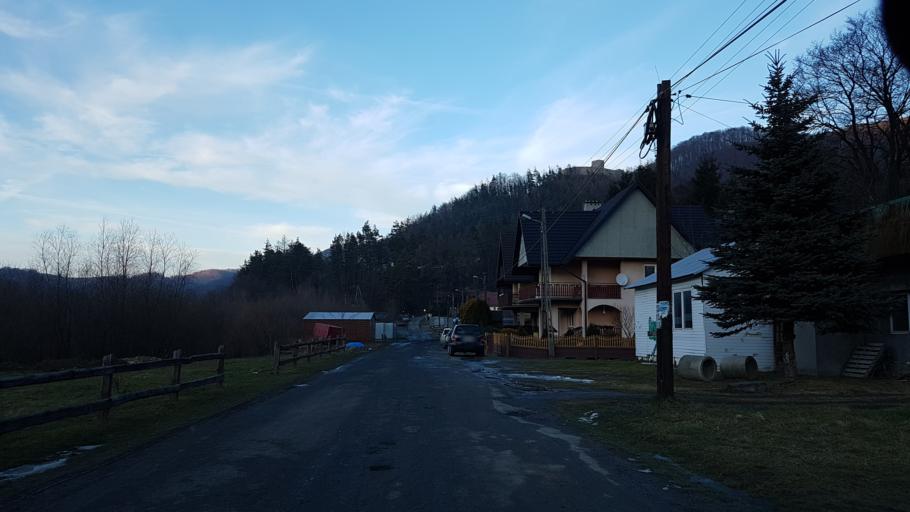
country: PL
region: Lesser Poland Voivodeship
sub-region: Powiat nowosadecki
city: Rytro
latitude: 49.4848
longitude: 20.6836
